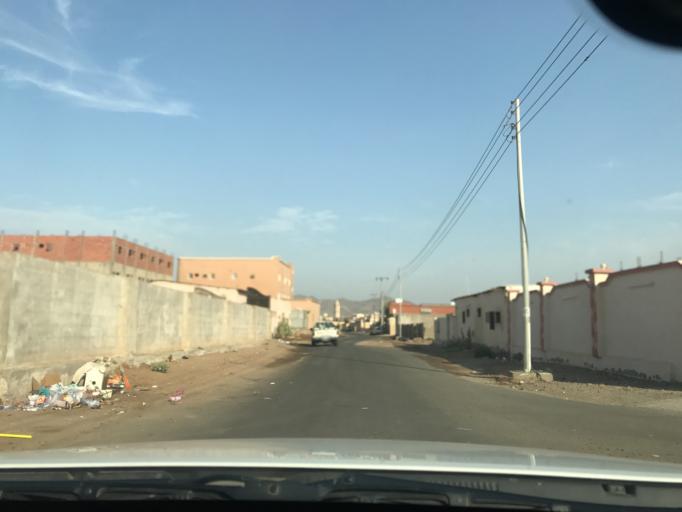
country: SA
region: Makkah
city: Al Jumum
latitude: 21.4423
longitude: 39.5196
